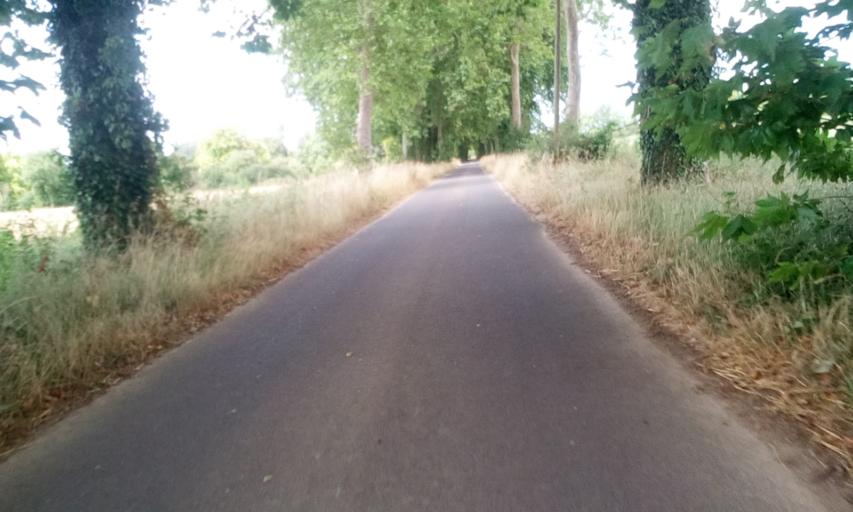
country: FR
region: Lower Normandy
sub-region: Departement du Calvados
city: Bellengreville
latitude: 49.1456
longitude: -0.2074
